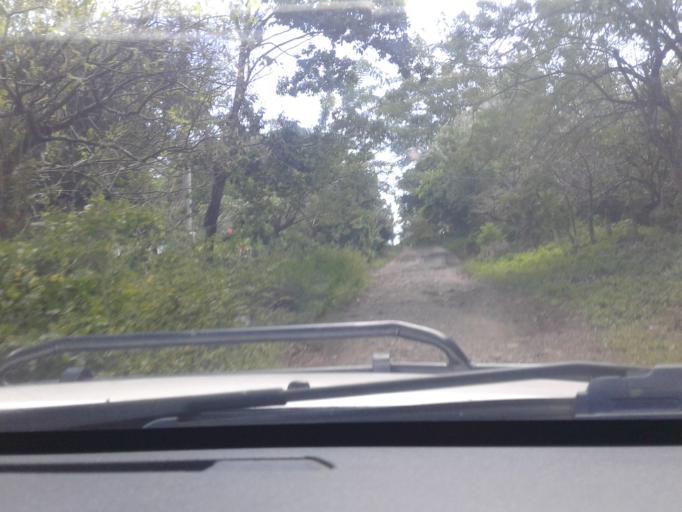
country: NI
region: Rivas
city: Altagracia
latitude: 11.4368
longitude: -85.5575
